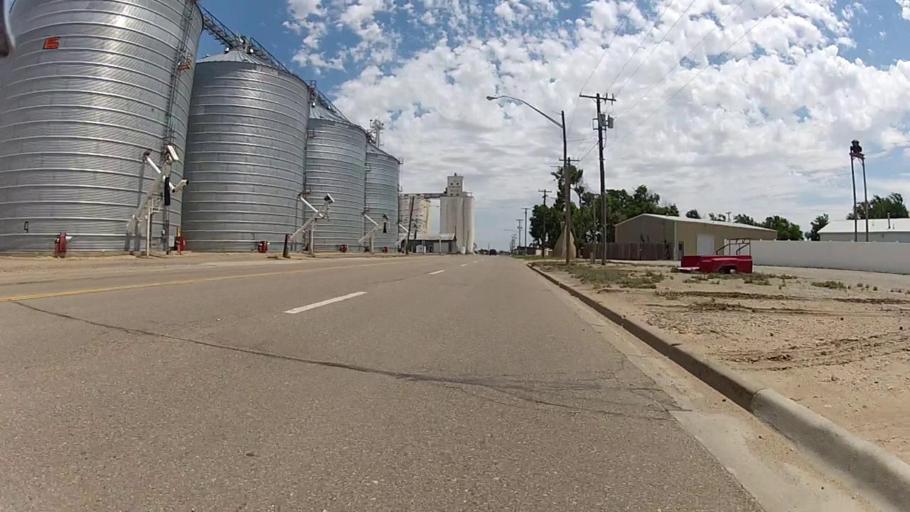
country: US
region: Kansas
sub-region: Haskell County
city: Satanta
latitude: 37.4389
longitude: -100.9903
